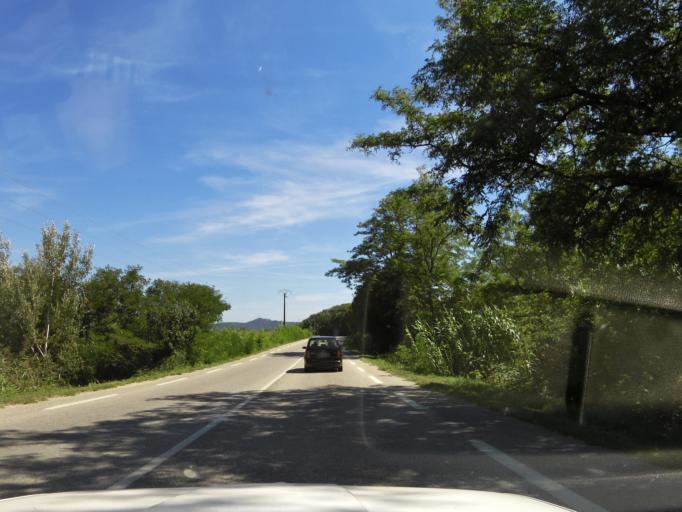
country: FR
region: Languedoc-Roussillon
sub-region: Departement du Gard
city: Bagnols-sur-Ceze
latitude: 44.1675
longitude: 4.5941
